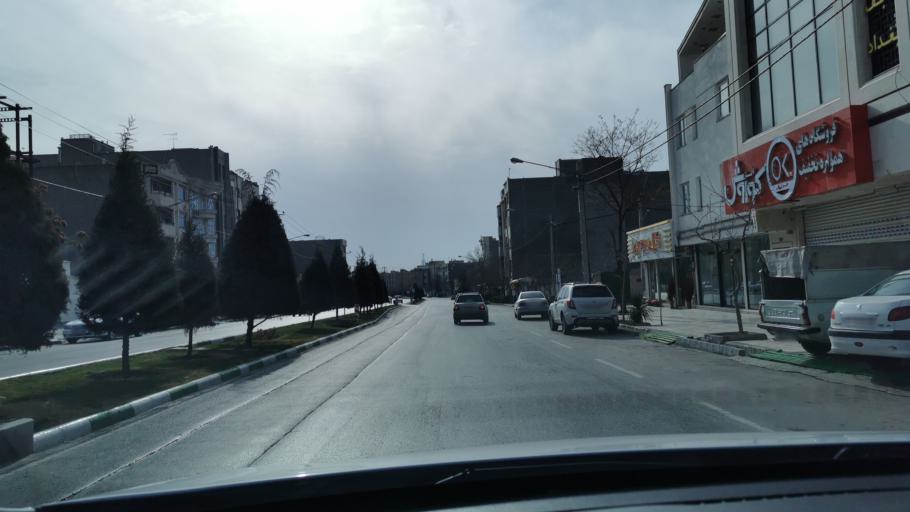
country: IR
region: Razavi Khorasan
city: Mashhad
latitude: 36.3154
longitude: 59.5098
